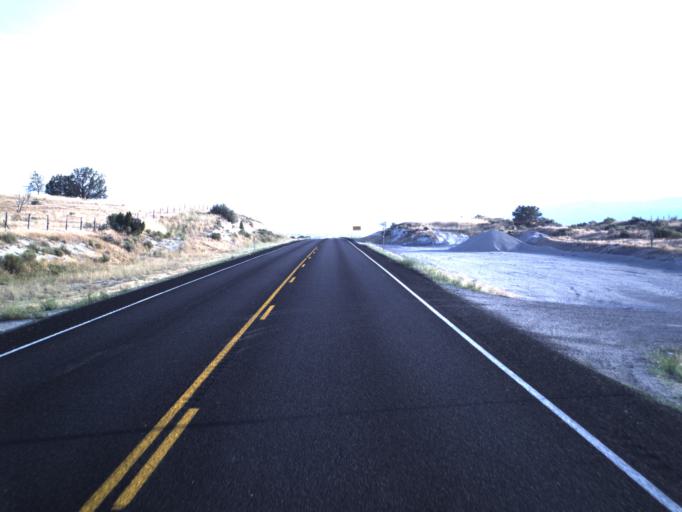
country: US
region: Utah
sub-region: Sanpete County
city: Moroni
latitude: 39.4789
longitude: -111.5238
